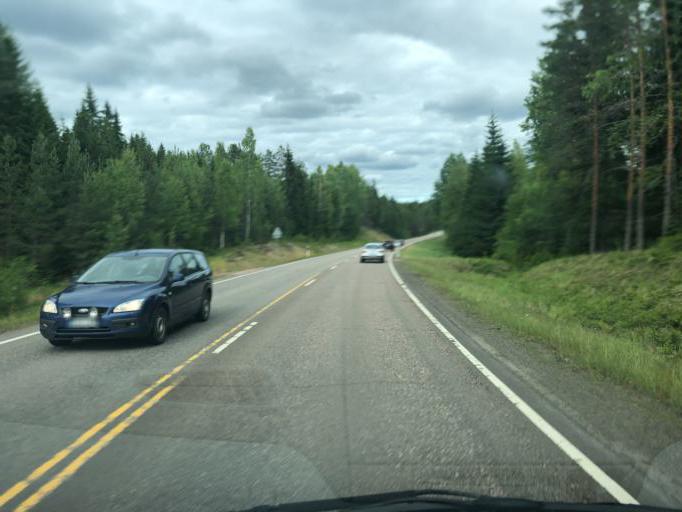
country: FI
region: Kymenlaakso
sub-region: Kouvola
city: Kouvola
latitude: 61.0390
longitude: 26.9913
